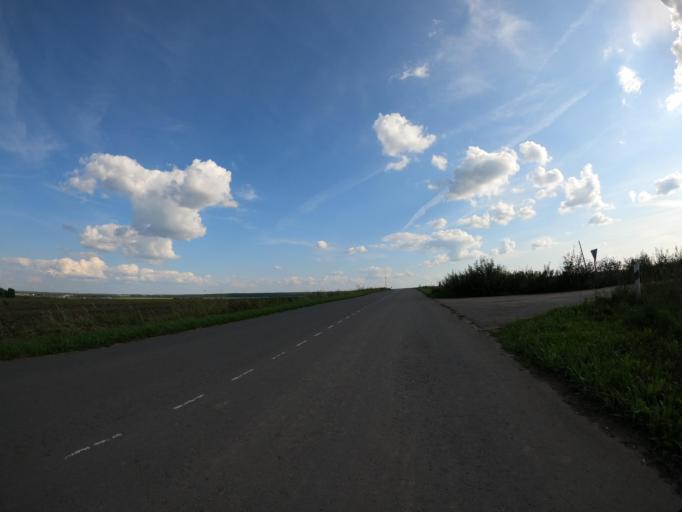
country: RU
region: Moskovskaya
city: Troitskoye
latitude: 55.2061
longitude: 38.4885
